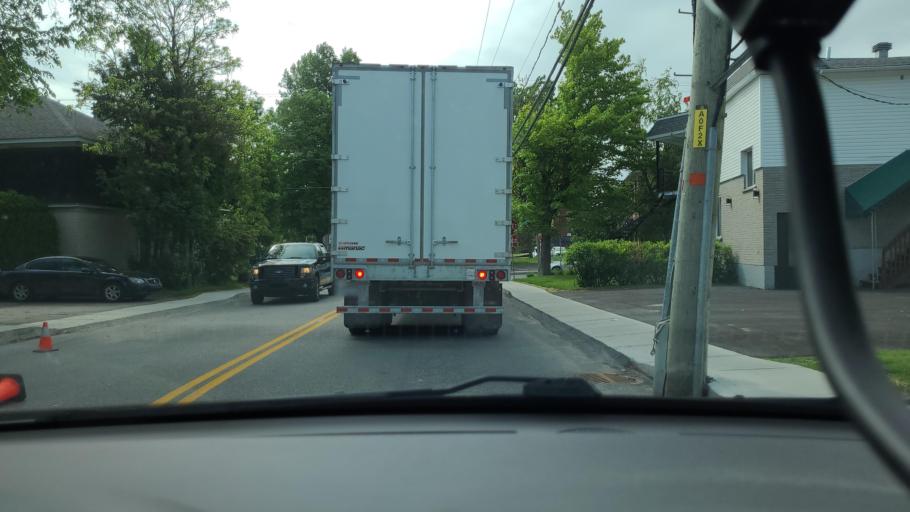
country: CA
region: Quebec
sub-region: Lanaudiere
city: Crabtree
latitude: 45.9647
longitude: -73.4746
